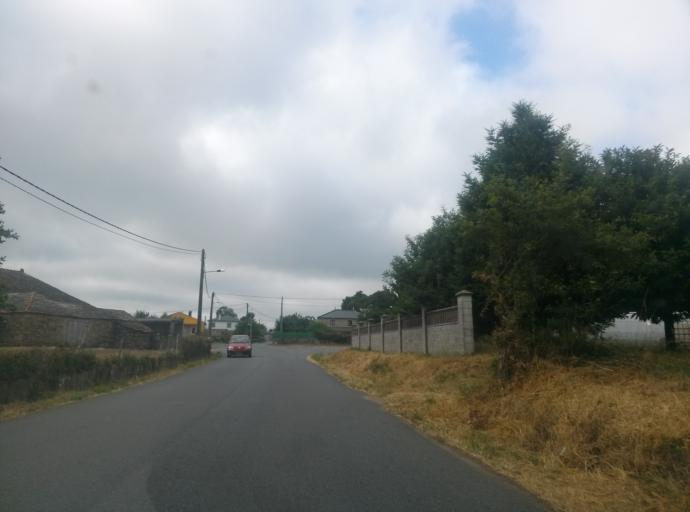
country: ES
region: Galicia
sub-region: Provincia de Lugo
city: Lugo
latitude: 43.0553
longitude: -7.5652
